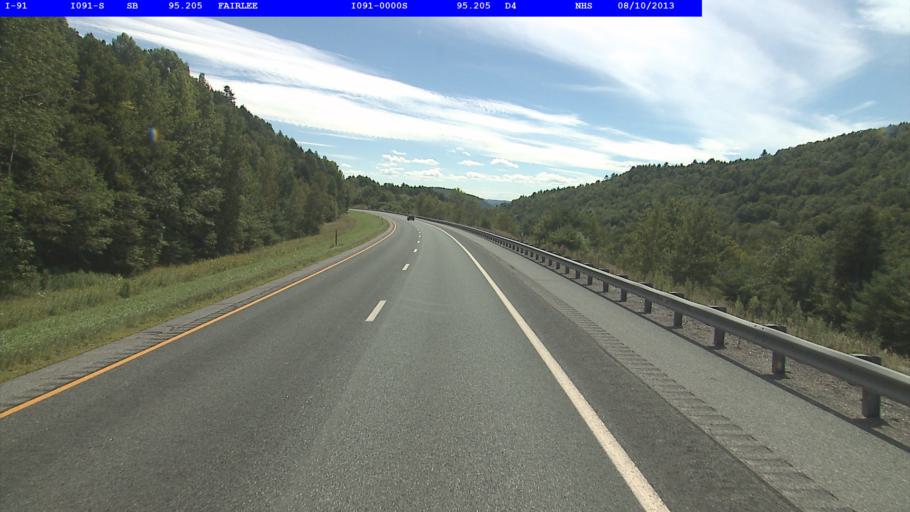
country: US
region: New Hampshire
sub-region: Grafton County
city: Orford
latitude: 43.9508
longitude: -72.1327
